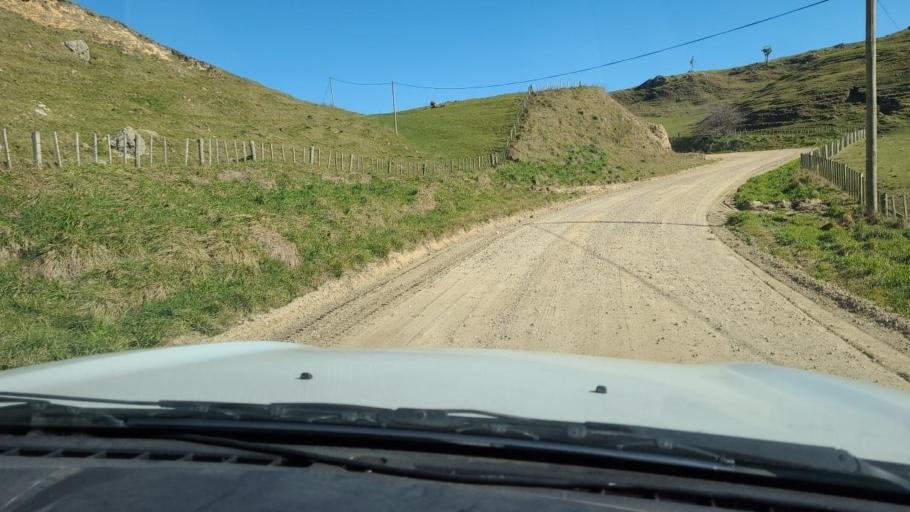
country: NZ
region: Hawke's Bay
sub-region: Hastings District
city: Hastings
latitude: -39.8114
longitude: 176.9651
